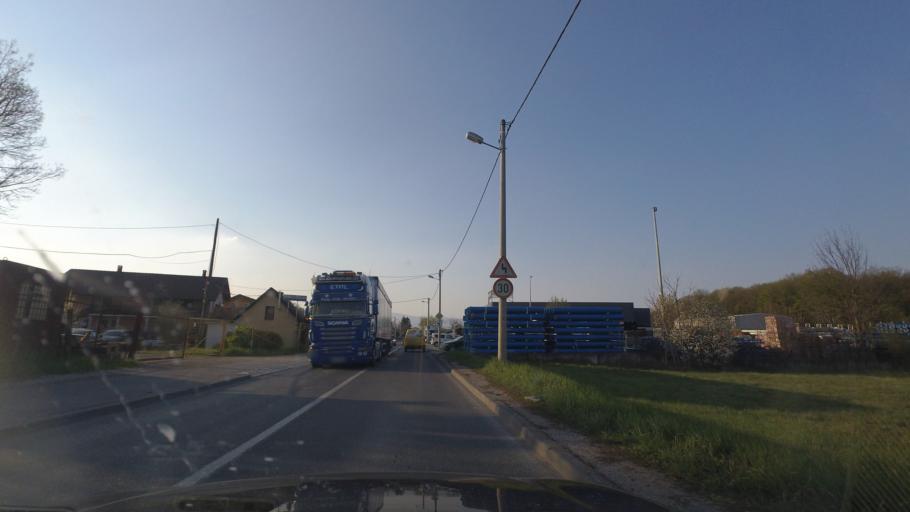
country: HR
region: Grad Zagreb
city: Dubrava
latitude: 45.8062
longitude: 16.0720
